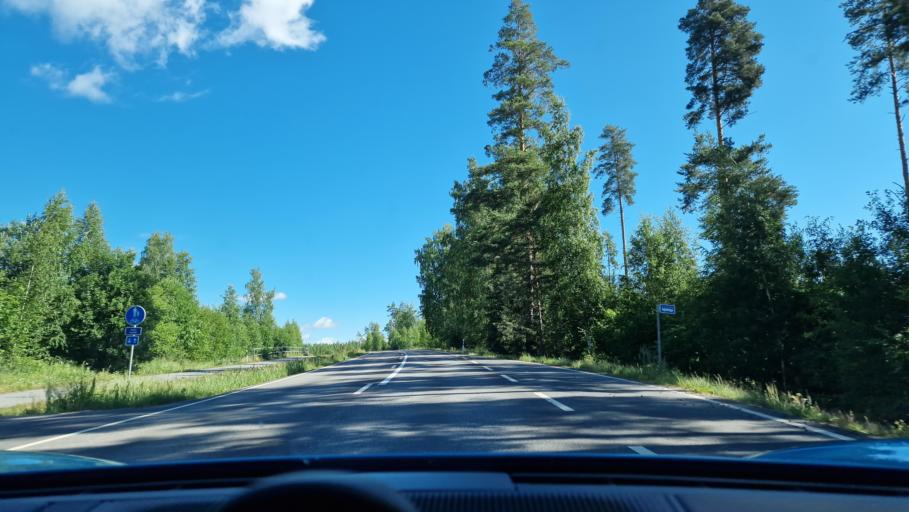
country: FI
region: Pirkanmaa
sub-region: Tampere
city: Kangasala
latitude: 61.4833
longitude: 24.1525
